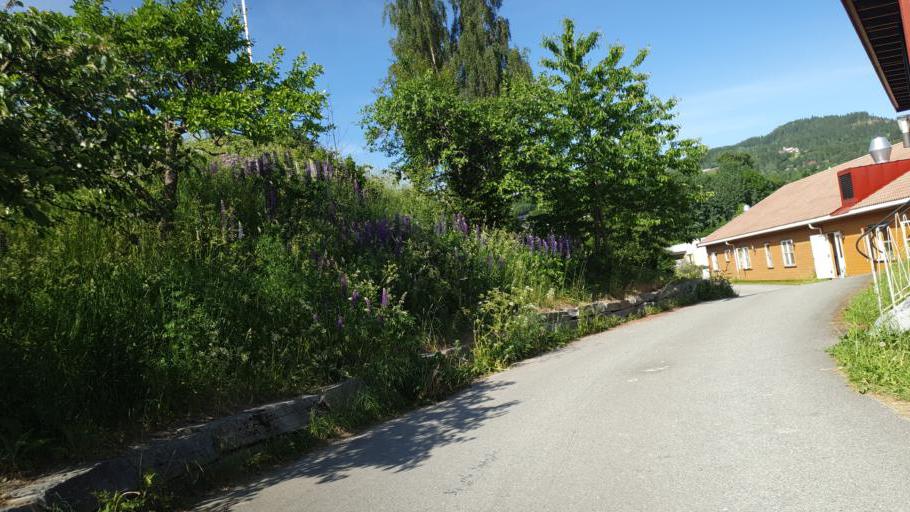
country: NO
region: Nord-Trondelag
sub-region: Leksvik
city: Leksvik
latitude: 63.6723
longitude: 10.6288
